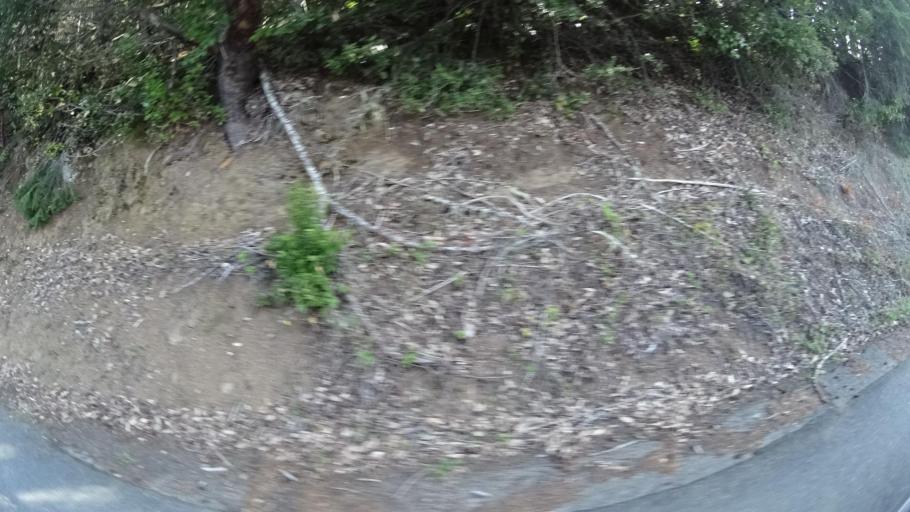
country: US
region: California
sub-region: Humboldt County
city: Hydesville
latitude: 40.6432
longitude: -123.9097
